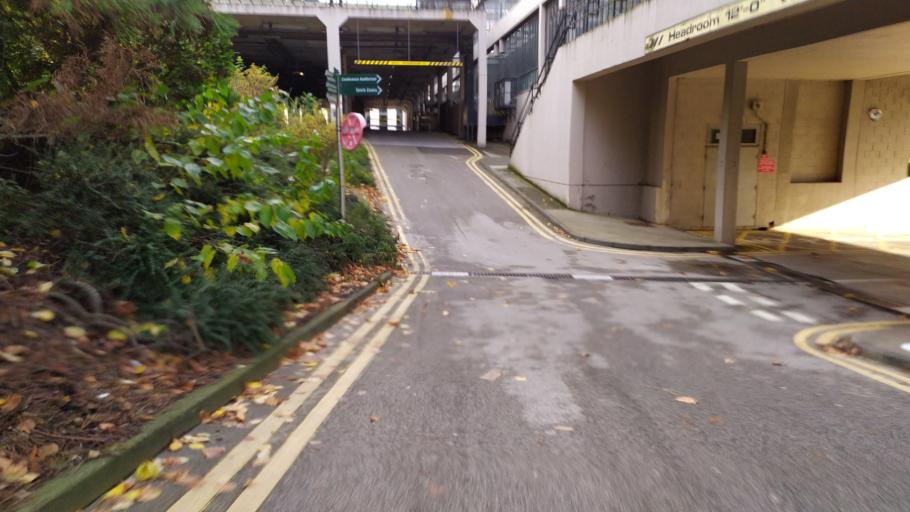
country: GB
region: England
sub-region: City and Borough of Leeds
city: Leeds
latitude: 53.8055
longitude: -1.5526
